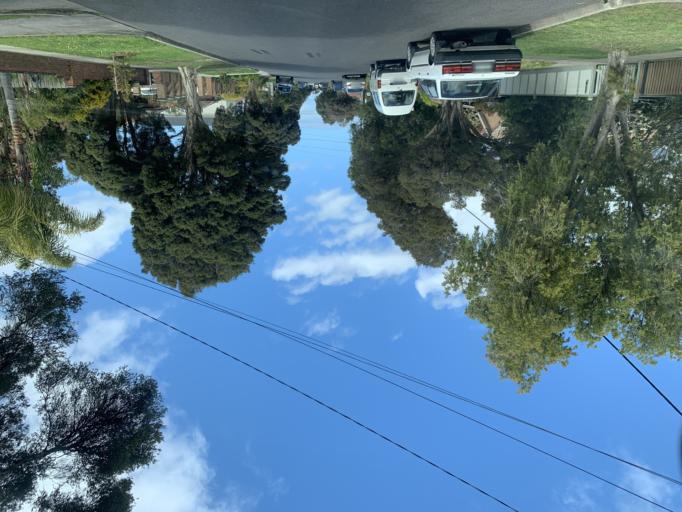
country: AU
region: Victoria
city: Thornbury
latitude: -37.7340
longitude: 144.9895
